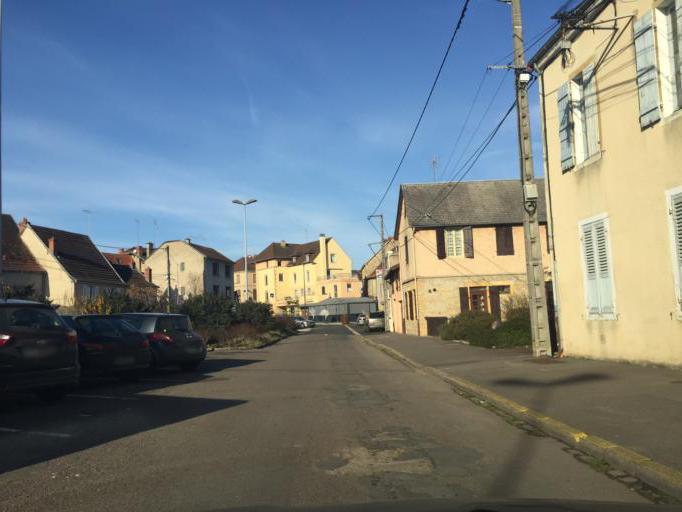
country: FR
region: Bourgogne
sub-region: Departement de Saone-et-Loire
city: Paray-le-Monial
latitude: 46.4489
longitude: 4.1198
